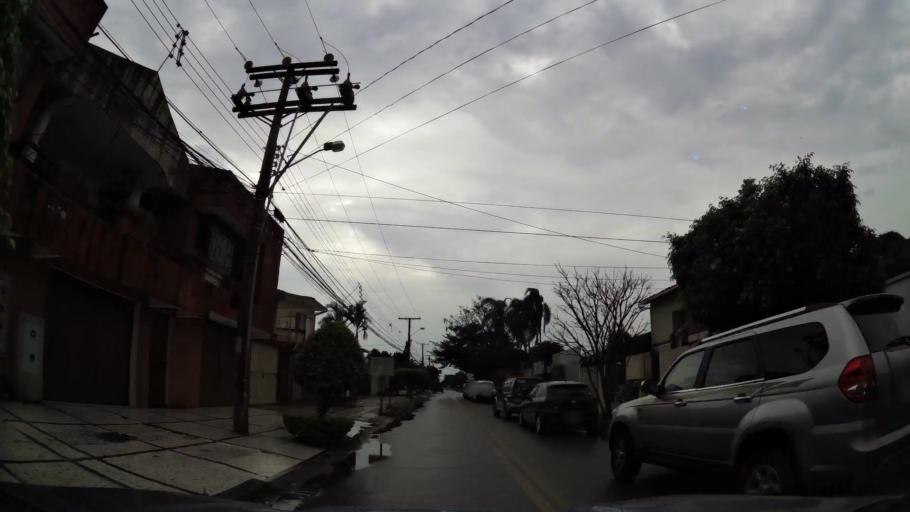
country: BO
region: Santa Cruz
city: Santa Cruz de la Sierra
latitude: -17.7656
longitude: -63.1573
